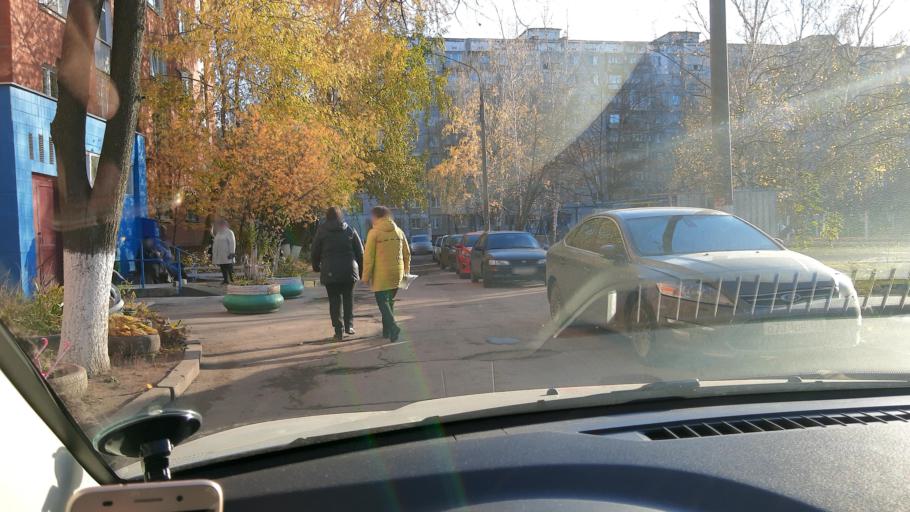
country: RU
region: Nizjnij Novgorod
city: Gorbatovka
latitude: 56.2627
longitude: 43.8544
